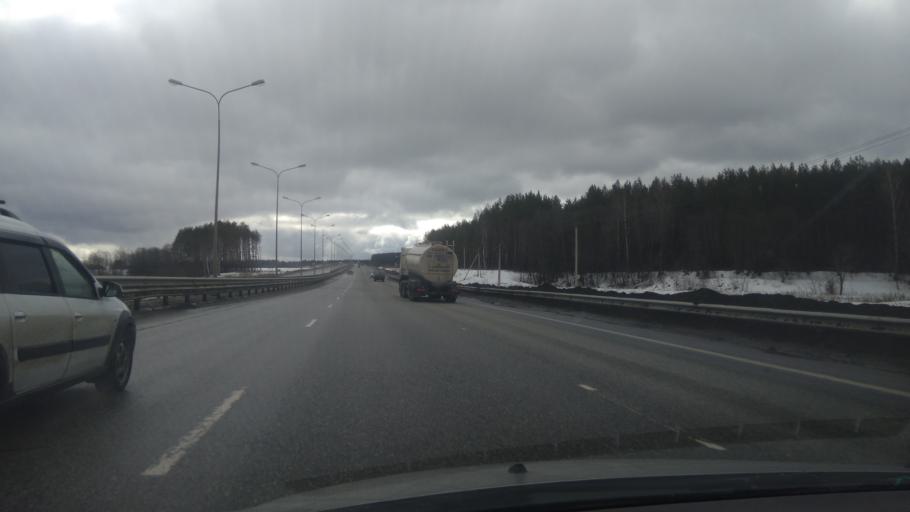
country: RU
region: Perm
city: Bershet'
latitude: 57.7206
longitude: 56.3564
